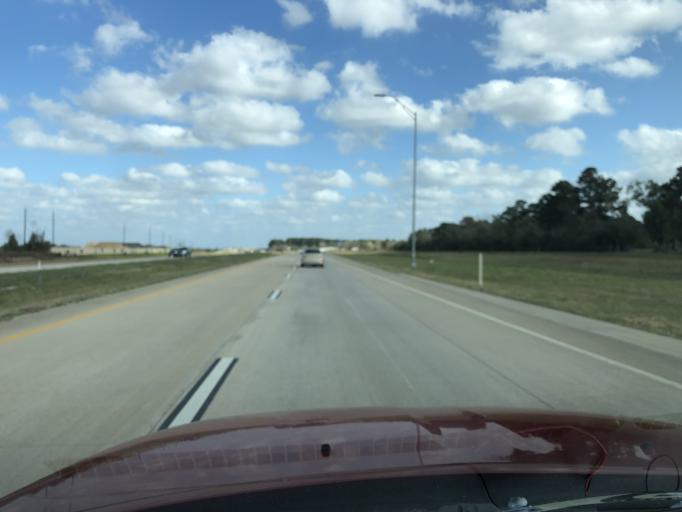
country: US
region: Texas
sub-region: Harris County
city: Cypress
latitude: 30.0533
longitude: -95.7276
